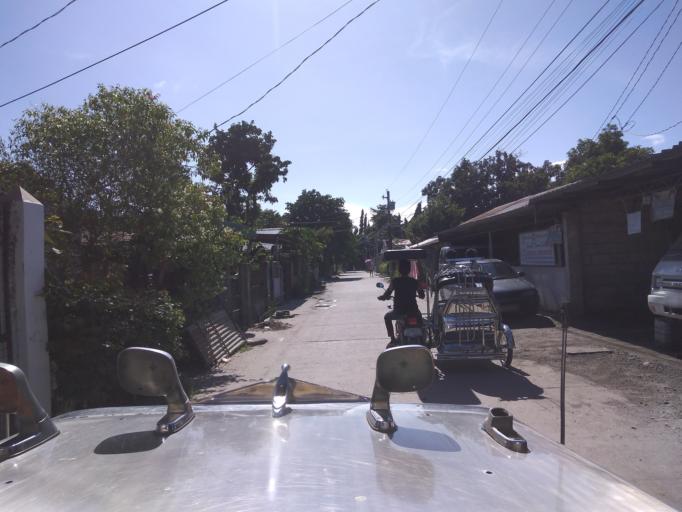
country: PH
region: Central Luzon
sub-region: Province of Pampanga
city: Calibutbut
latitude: 15.1002
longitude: 120.6053
